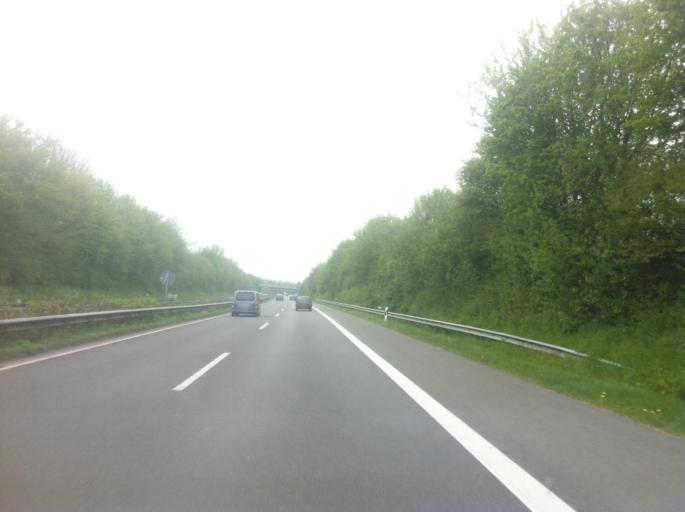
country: DE
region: North Rhine-Westphalia
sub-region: Regierungsbezirk Detmold
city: Oerlinghausen
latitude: 51.9851
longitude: 8.6431
